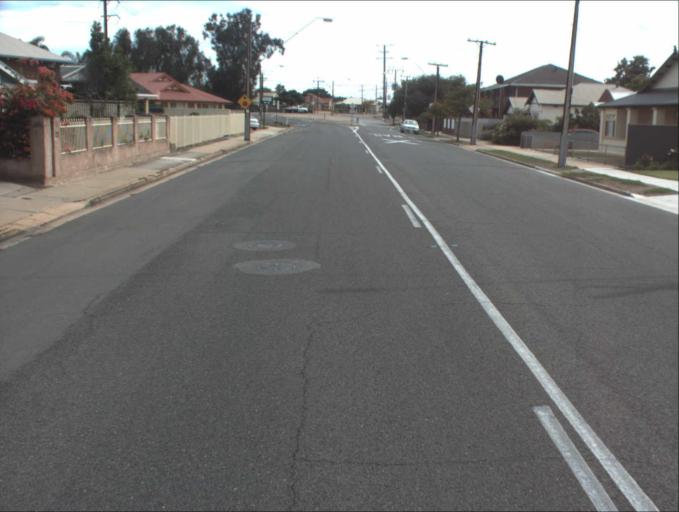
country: AU
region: South Australia
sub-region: Port Adelaide Enfield
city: Birkenhead
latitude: -34.8202
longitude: 138.4941
